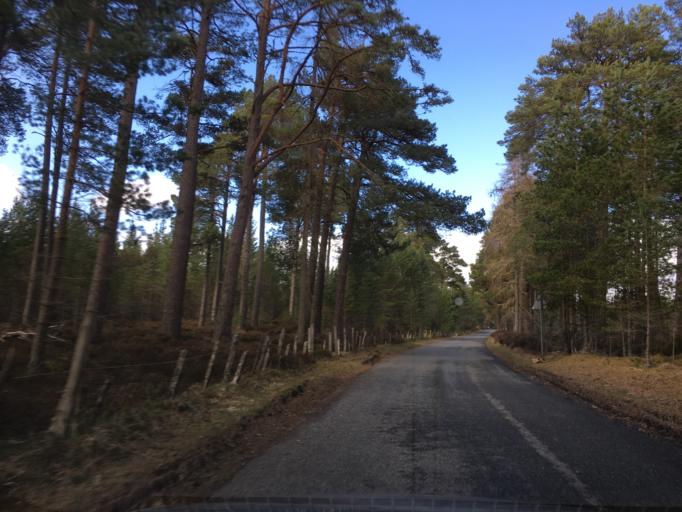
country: GB
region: Scotland
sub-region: Highland
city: Aviemore
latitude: 57.1781
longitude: -3.7978
